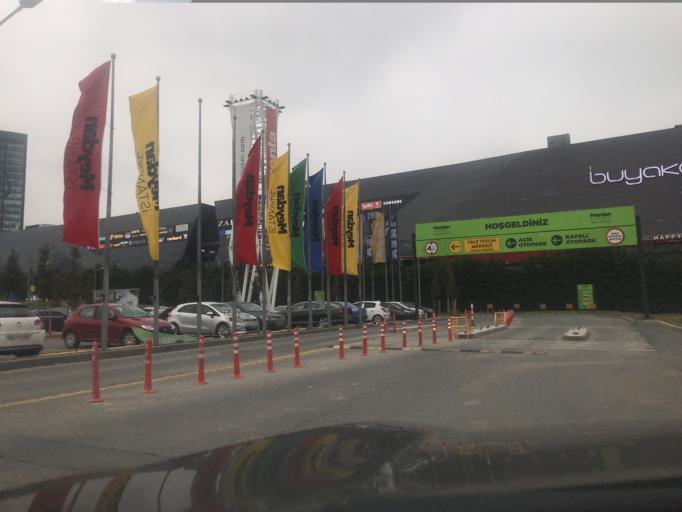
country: TR
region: Istanbul
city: Umraniye
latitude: 41.0253
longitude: 29.1284
